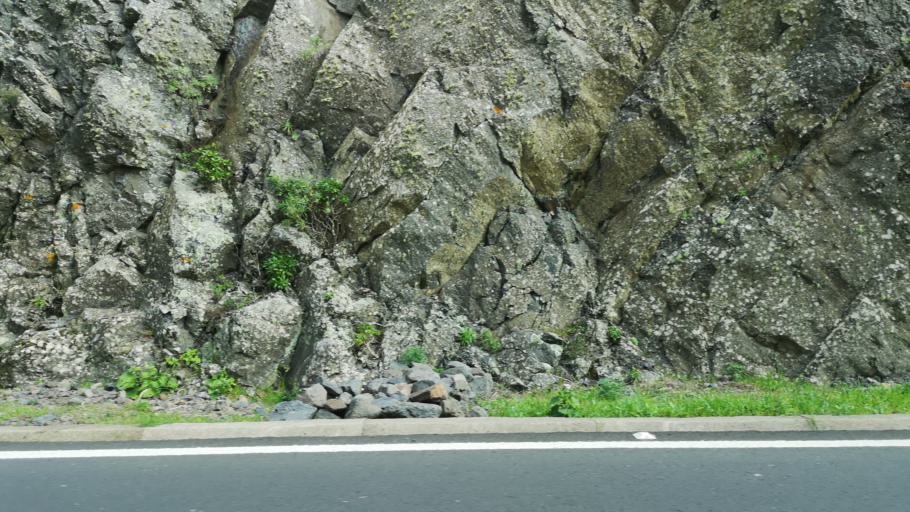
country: ES
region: Canary Islands
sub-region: Provincia de Santa Cruz de Tenerife
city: Alajero
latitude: 28.1033
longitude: -17.2093
